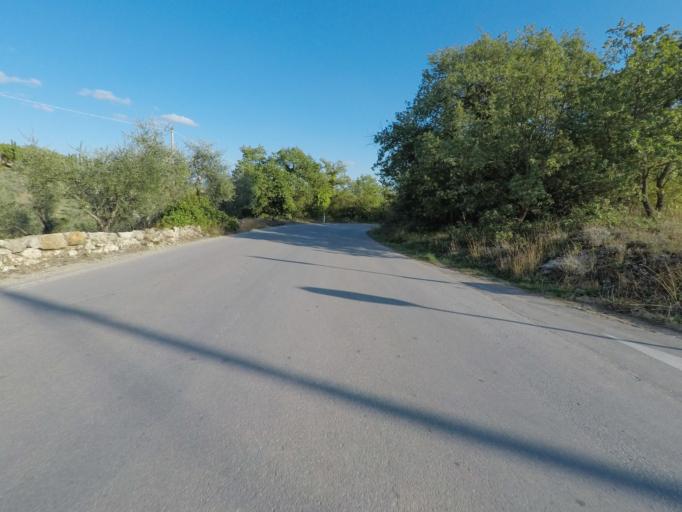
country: IT
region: Tuscany
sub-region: Provincia di Siena
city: Radda in Chianti
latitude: 43.4514
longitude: 11.3907
